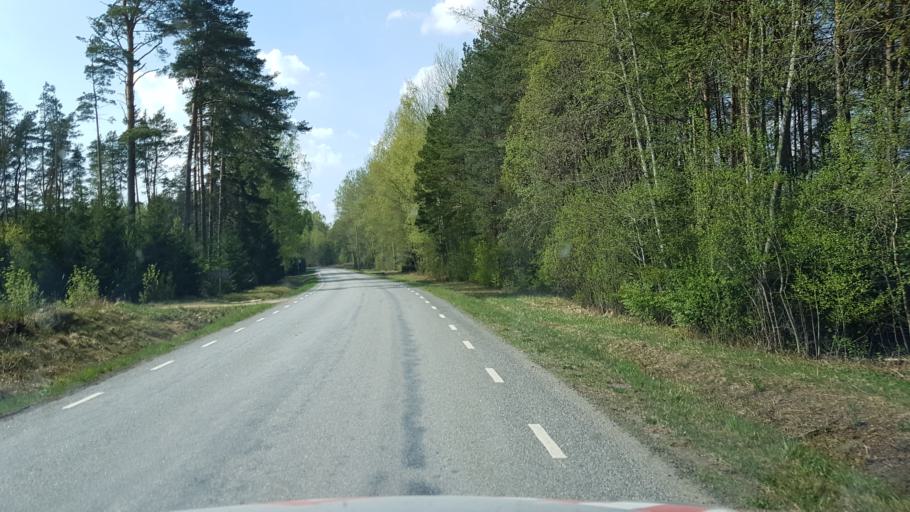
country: EE
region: Paernumaa
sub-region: Paikuse vald
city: Paikuse
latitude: 58.4439
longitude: 24.5932
